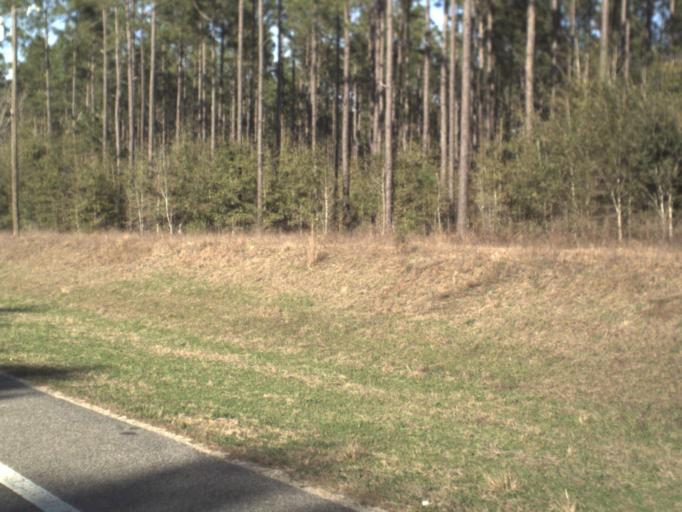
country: US
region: Florida
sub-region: Jackson County
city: Marianna
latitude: 30.5887
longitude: -85.1818
